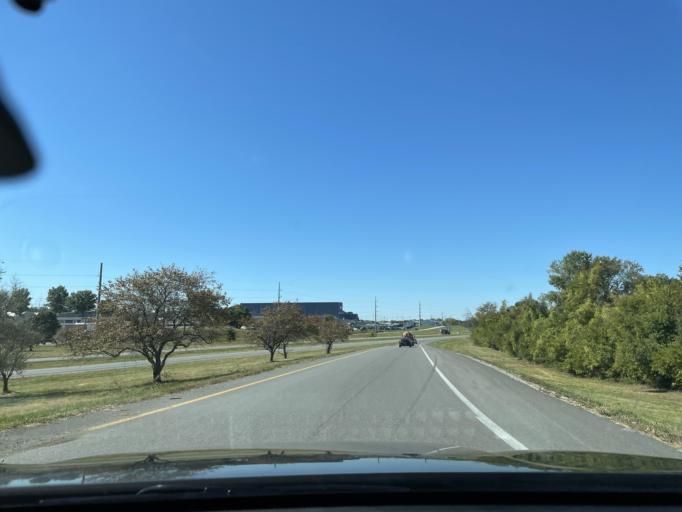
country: US
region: Missouri
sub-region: Buchanan County
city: Saint Joseph
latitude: 39.7505
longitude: -94.7684
